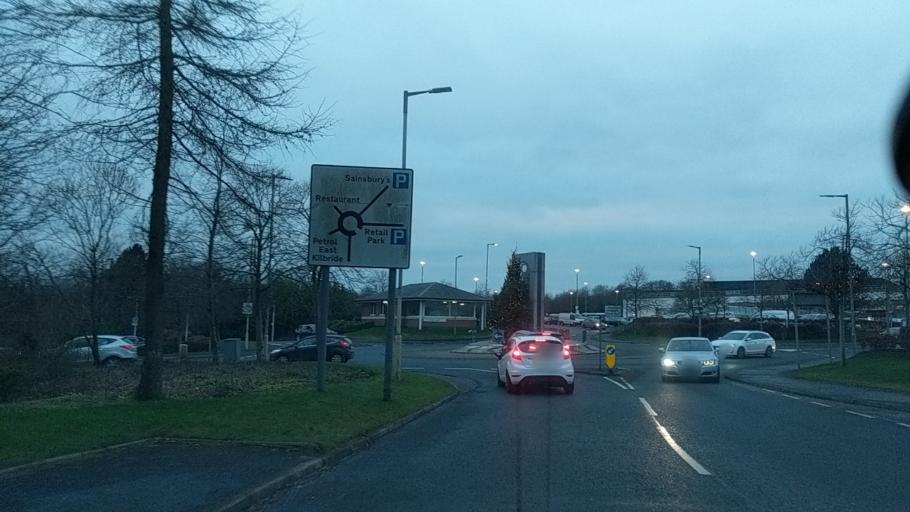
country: GB
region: Scotland
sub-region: South Lanarkshire
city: East Kilbride
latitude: 55.7834
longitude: -4.1672
